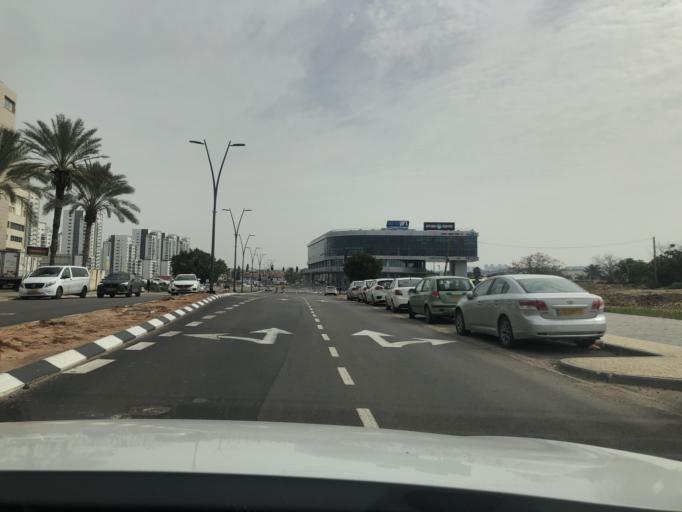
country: IL
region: Central District
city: Rosh Ha'Ayin
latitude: 32.1055
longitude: 34.9400
